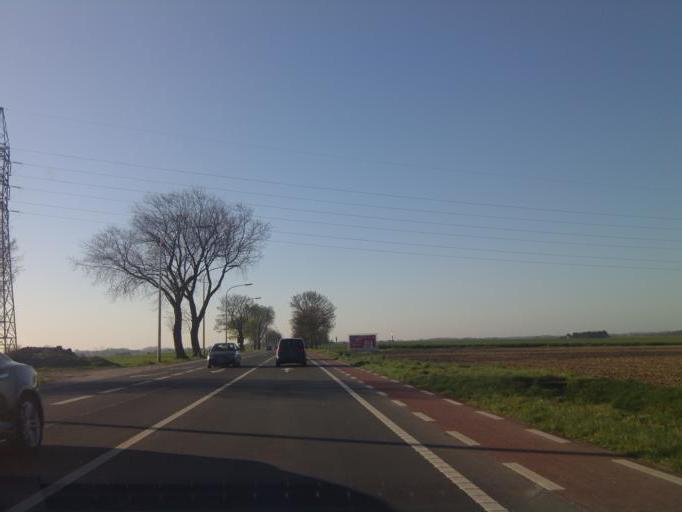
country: BE
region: Wallonia
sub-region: Province du Brabant Wallon
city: Louvain-la-Neuve
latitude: 50.6557
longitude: 4.6371
